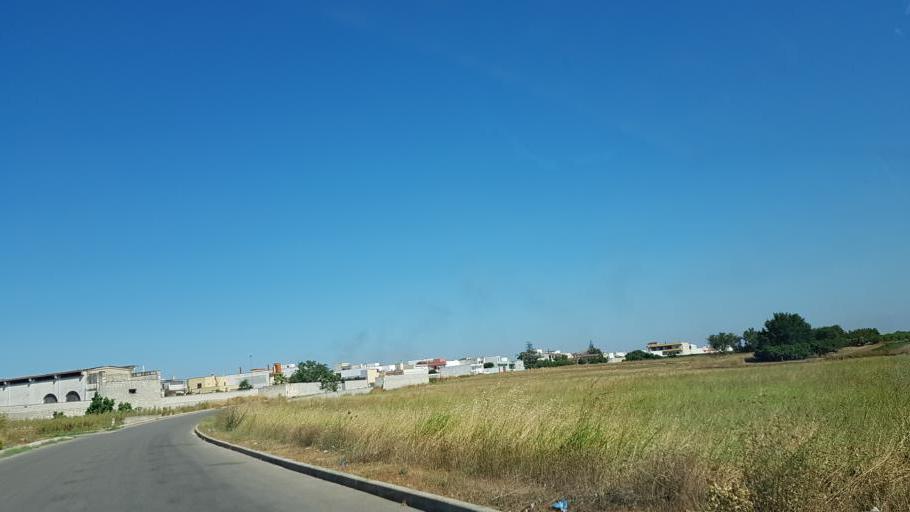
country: IT
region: Apulia
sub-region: Provincia di Brindisi
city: San Donaci
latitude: 40.4448
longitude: 17.9214
